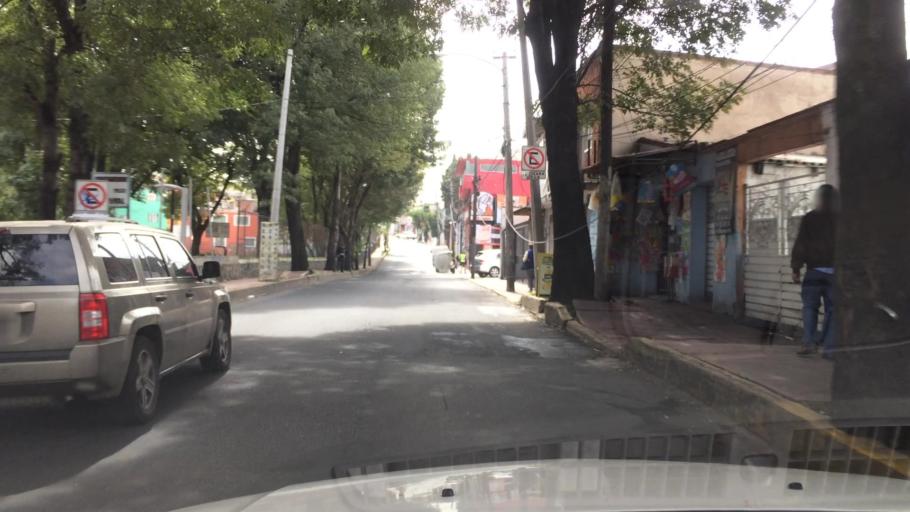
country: MX
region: Mexico City
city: Tlalpan
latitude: 19.2807
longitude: -99.1374
